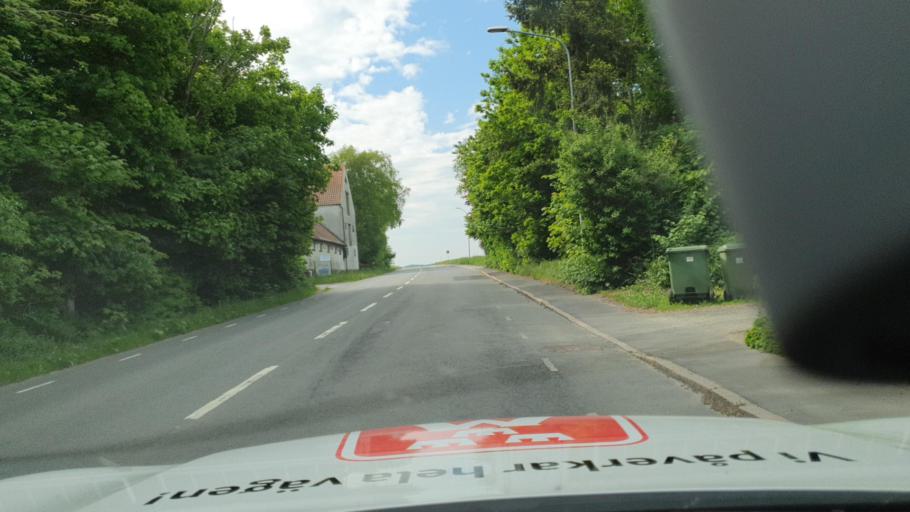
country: SE
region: Skane
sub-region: Simrishamns Kommun
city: Kivik
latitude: 55.5538
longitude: 14.1707
